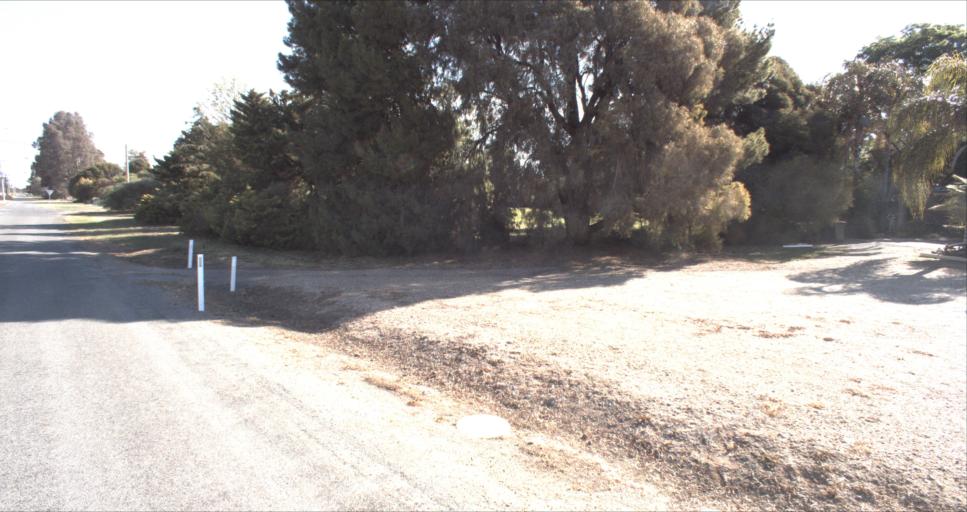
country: AU
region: New South Wales
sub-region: Leeton
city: Leeton
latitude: -34.5428
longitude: 146.4152
